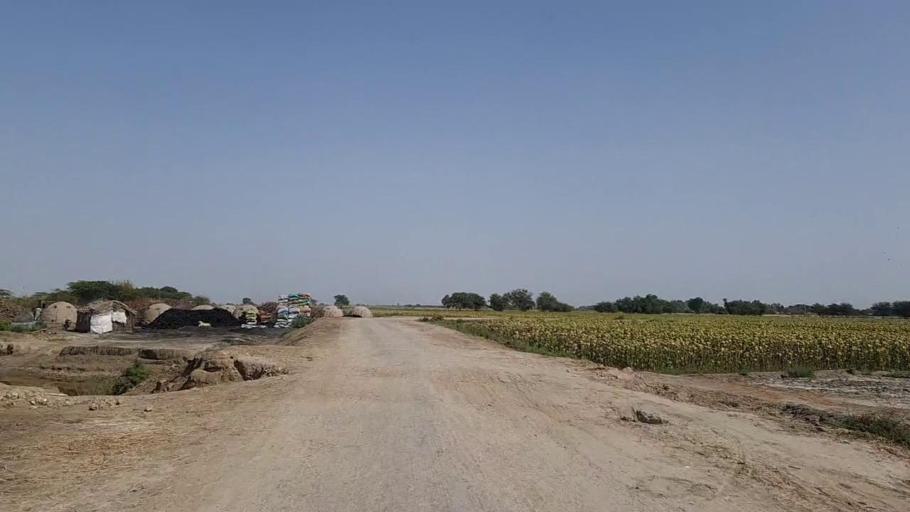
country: PK
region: Sindh
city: Jati
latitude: 24.3539
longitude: 68.2755
